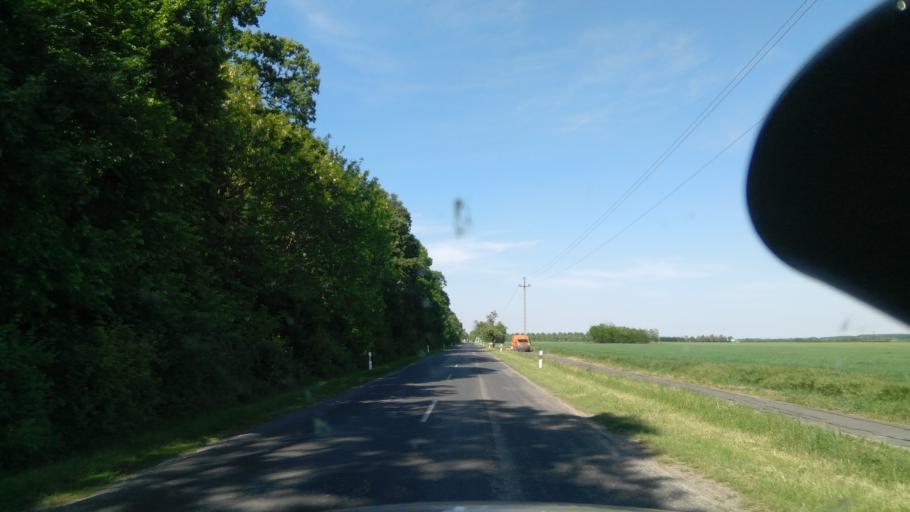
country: HU
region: Bekes
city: Sarkad
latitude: 46.7130
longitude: 21.3265
